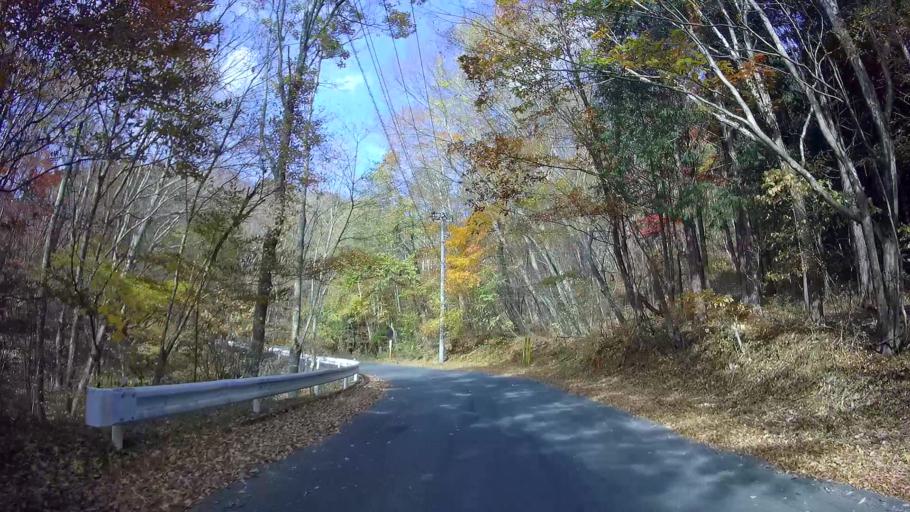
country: JP
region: Gunma
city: Nakanojomachi
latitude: 36.5171
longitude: 138.6673
